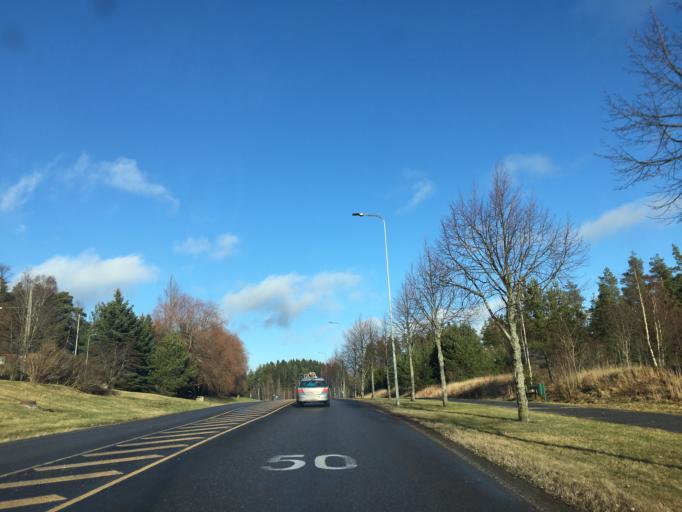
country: FI
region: Varsinais-Suomi
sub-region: Turku
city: Raisio
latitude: 60.4982
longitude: 22.1417
